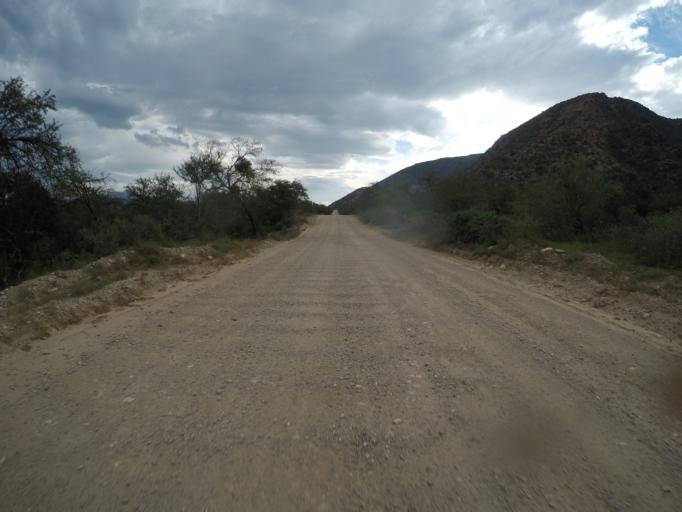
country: ZA
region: Eastern Cape
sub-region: Cacadu District Municipality
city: Kareedouw
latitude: -33.5728
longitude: 24.1297
